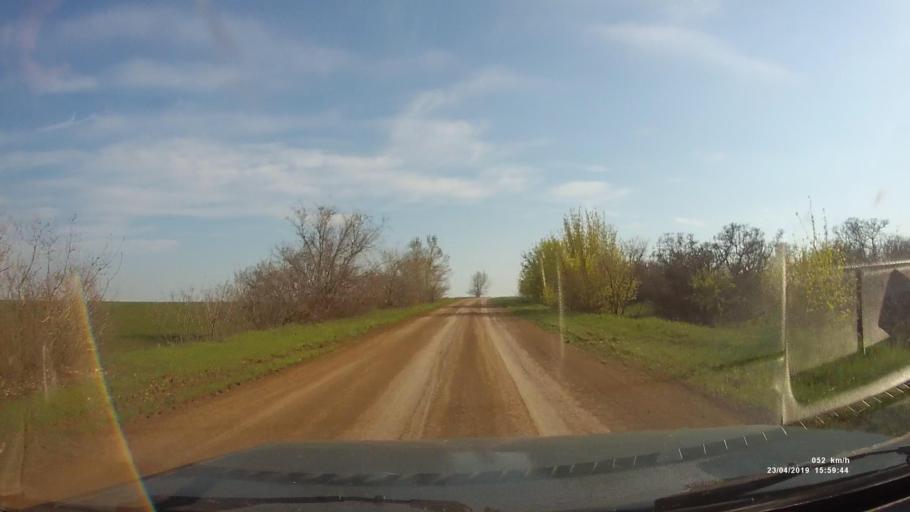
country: RU
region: Rostov
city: Remontnoye
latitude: 46.5145
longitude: 43.1095
